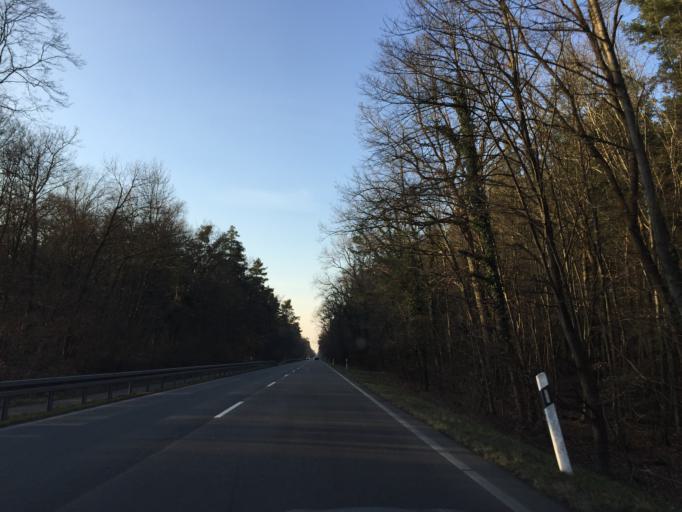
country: DE
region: Baden-Wuerttemberg
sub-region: Karlsruhe Region
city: Oftersheim
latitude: 49.3372
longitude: 8.6107
